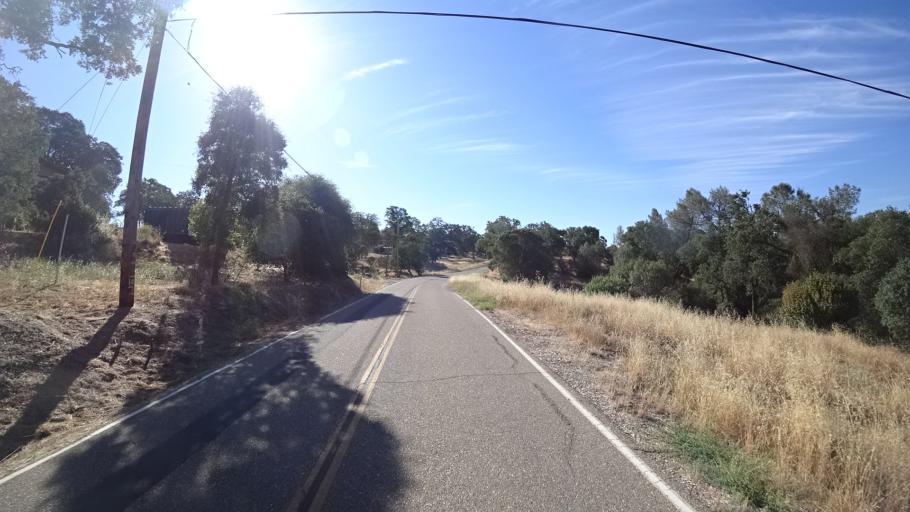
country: US
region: California
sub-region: Calaveras County
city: San Andreas
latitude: 38.1851
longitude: -120.6581
